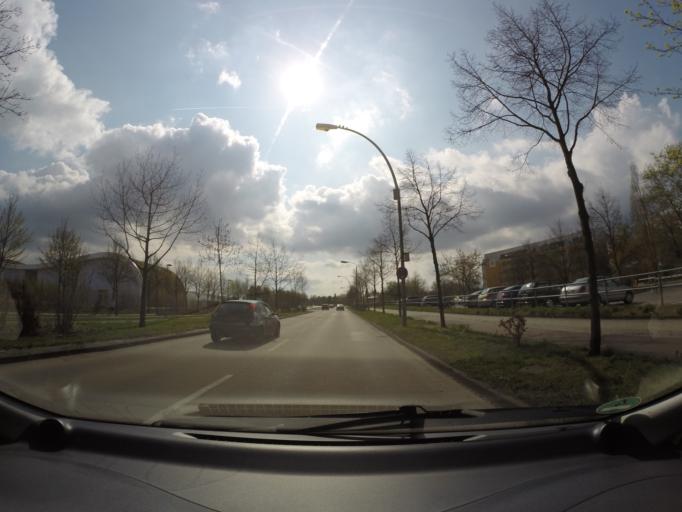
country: DE
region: Berlin
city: Marzahn
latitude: 52.5376
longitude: 13.5784
